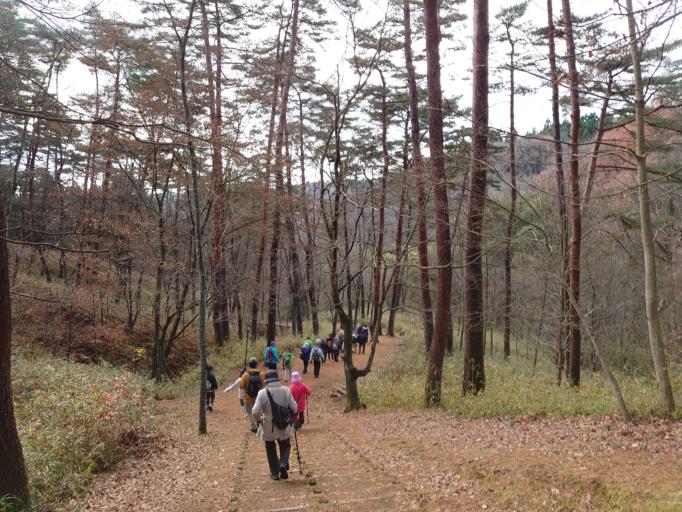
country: JP
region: Iwate
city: Ichinoseki
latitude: 38.9916
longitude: 141.1030
